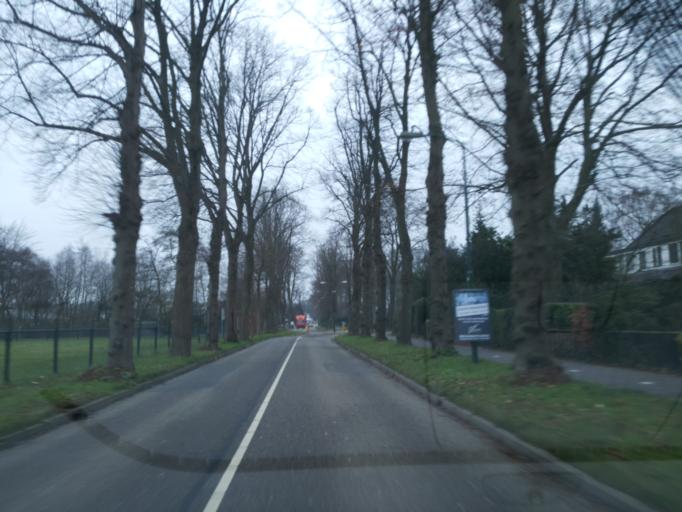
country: NL
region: North Holland
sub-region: Gemeente Wijdemeren
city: Nieuw-Loosdrecht
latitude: 52.2048
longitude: 5.1425
